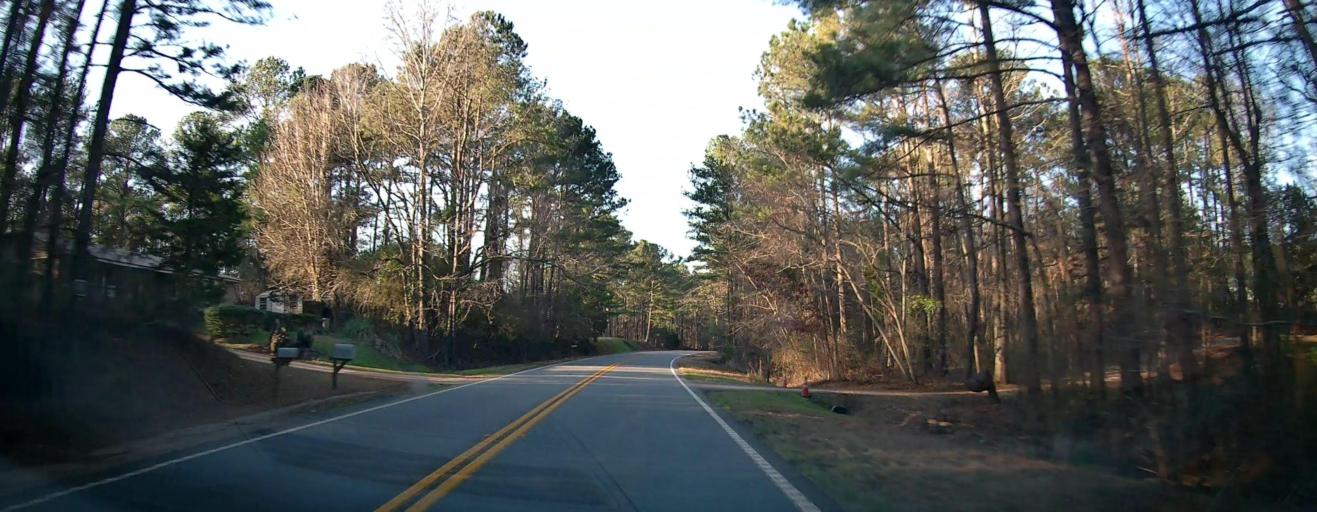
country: US
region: Alabama
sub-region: Chambers County
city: Valley
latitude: 32.7463
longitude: -85.0803
